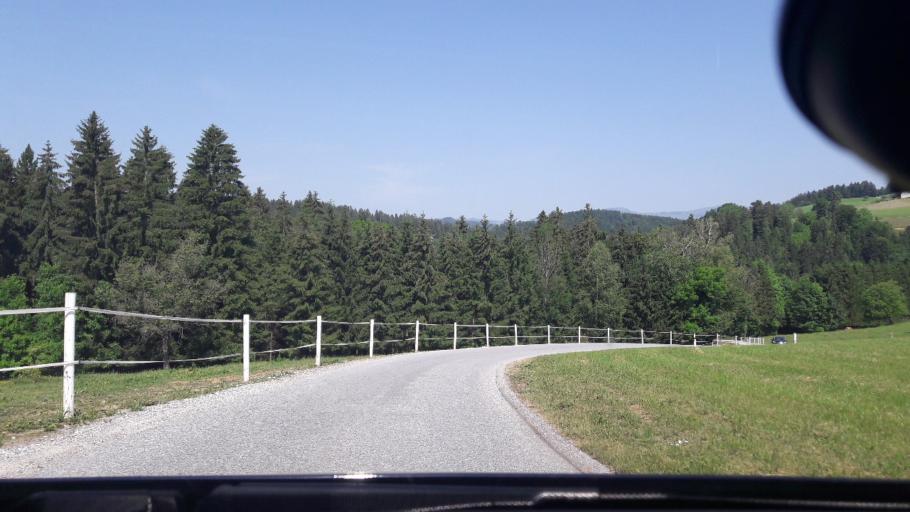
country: AT
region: Styria
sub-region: Politischer Bezirk Graz-Umgebung
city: Stiwoll
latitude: 47.1074
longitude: 15.1968
